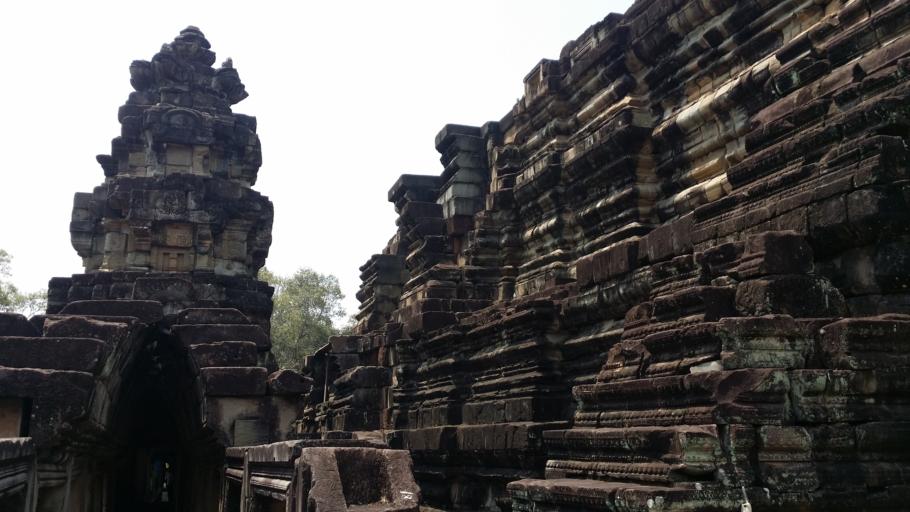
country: KH
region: Siem Reap
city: Siem Reap
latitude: 13.4440
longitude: 103.8562
